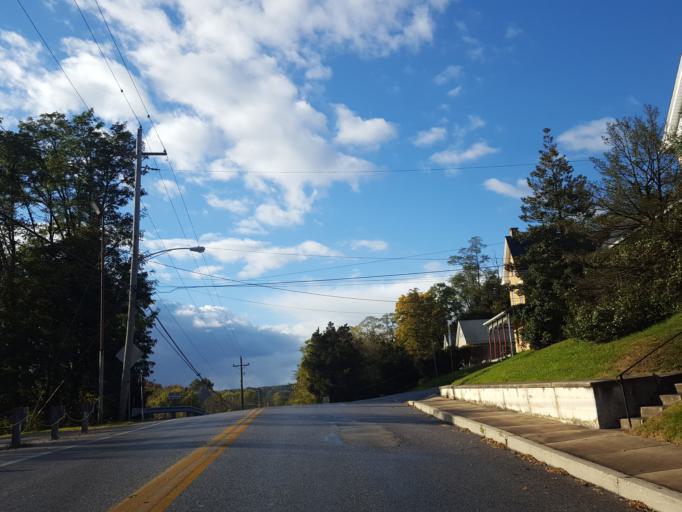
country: US
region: Pennsylvania
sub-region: York County
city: Yoe
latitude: 39.9110
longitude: -76.6365
